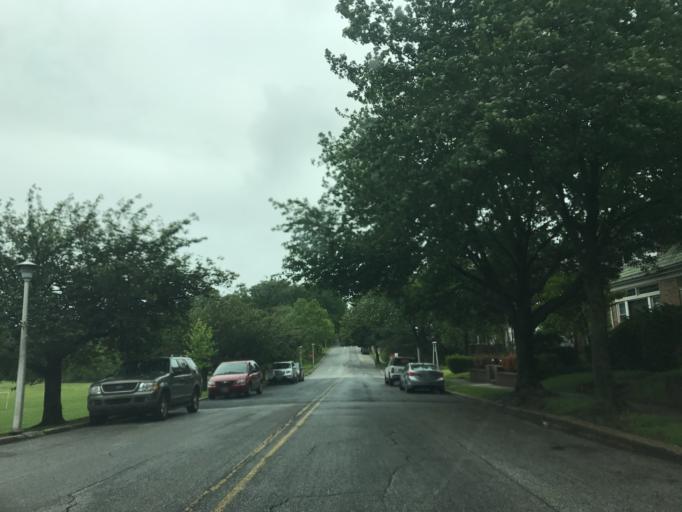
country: US
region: Maryland
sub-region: City of Baltimore
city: Baltimore
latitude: 39.3304
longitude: -76.5780
